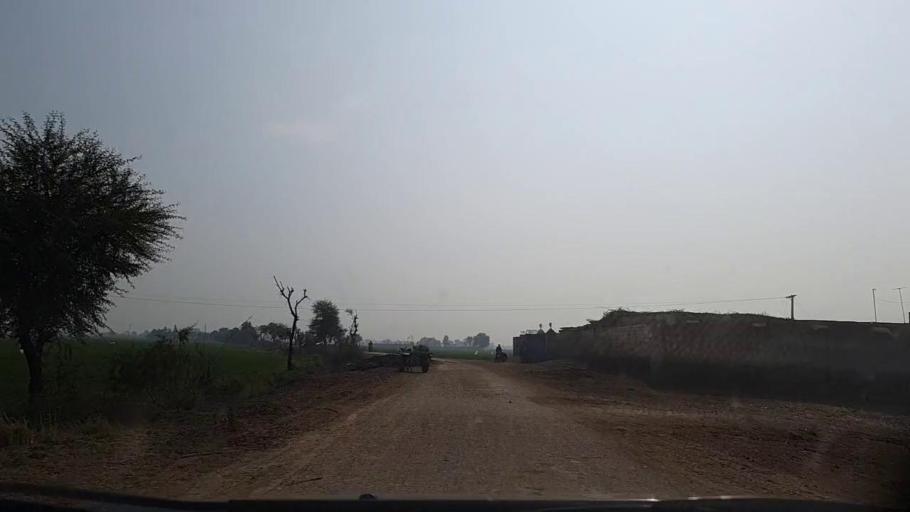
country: PK
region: Sindh
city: Sanghar
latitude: 26.0526
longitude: 68.9740
